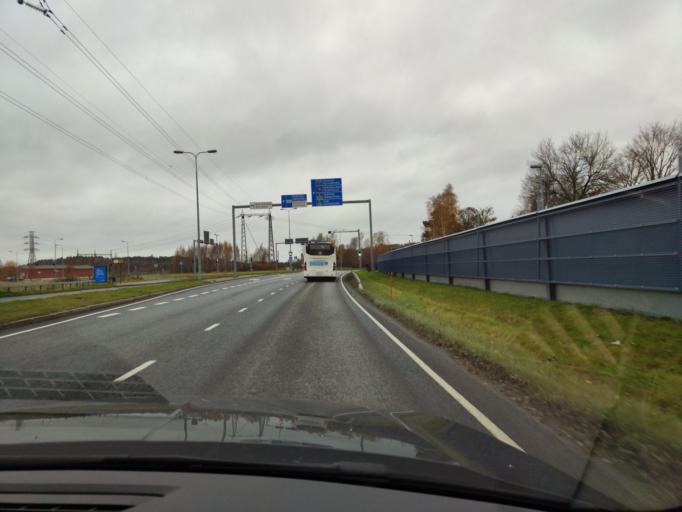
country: FI
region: Varsinais-Suomi
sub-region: Turku
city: Raisio
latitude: 60.4558
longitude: 22.1945
